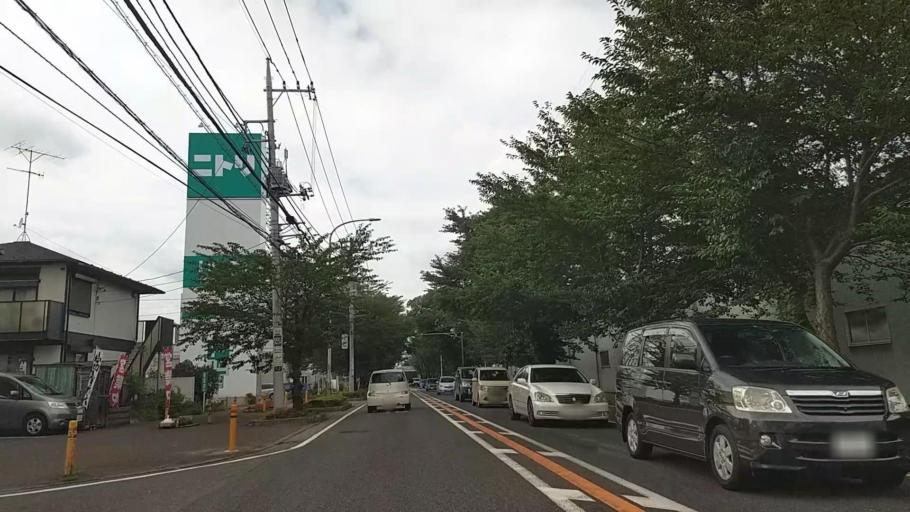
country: JP
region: Kanagawa
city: Minami-rinkan
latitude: 35.4379
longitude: 139.4670
